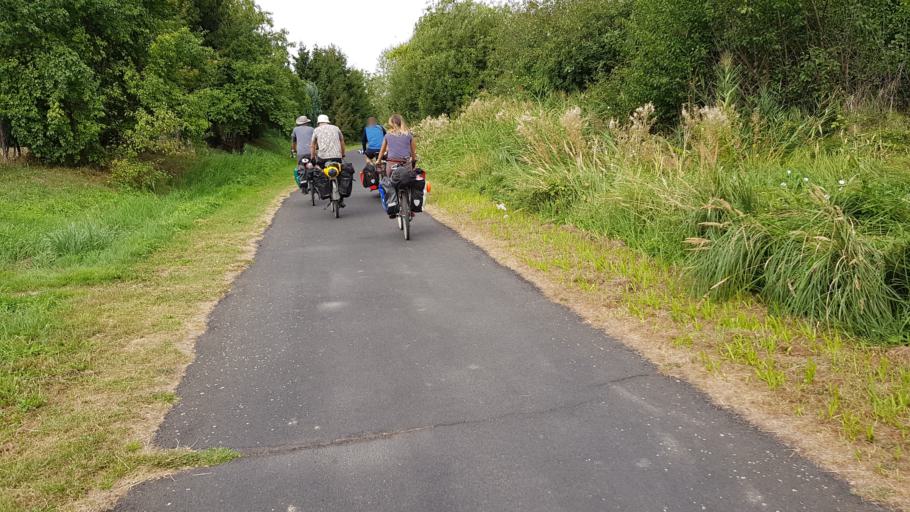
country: PL
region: West Pomeranian Voivodeship
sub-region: Powiat pyrzycki
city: Pyrzyce
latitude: 53.1495
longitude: 14.9022
